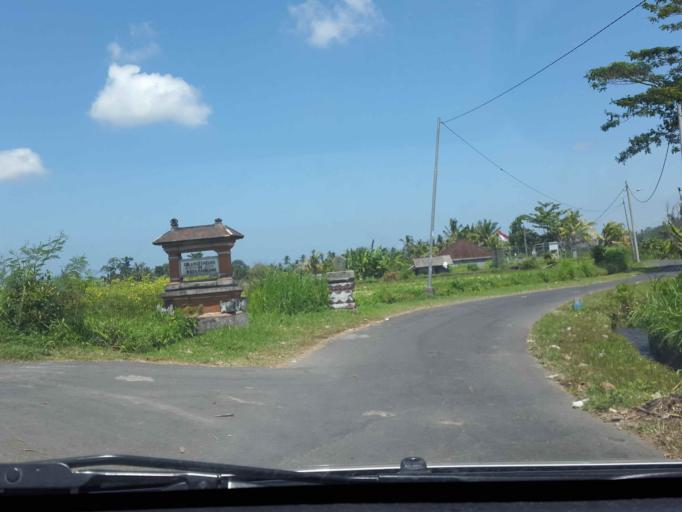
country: ID
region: Bali
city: Banjar Kelodan
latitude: -8.5041
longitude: 115.3933
